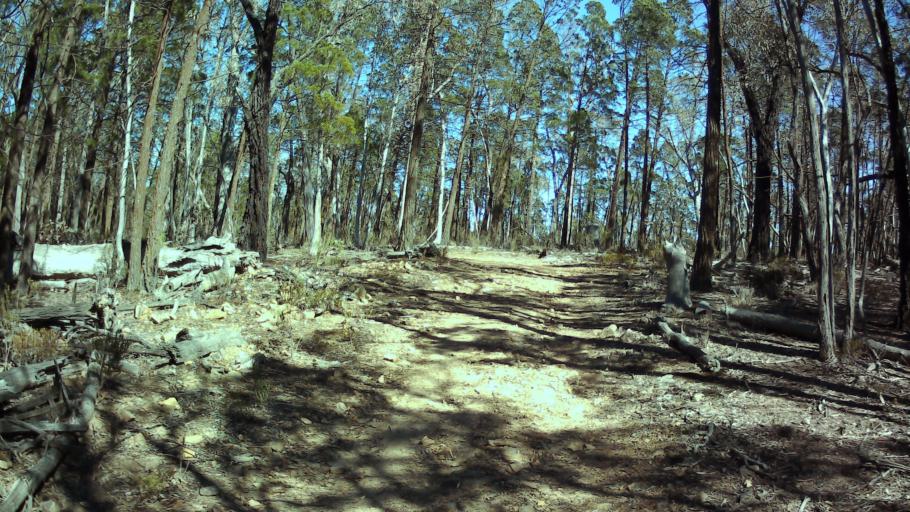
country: AU
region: New South Wales
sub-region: Weddin
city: Grenfell
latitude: -33.7383
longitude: 148.3638
